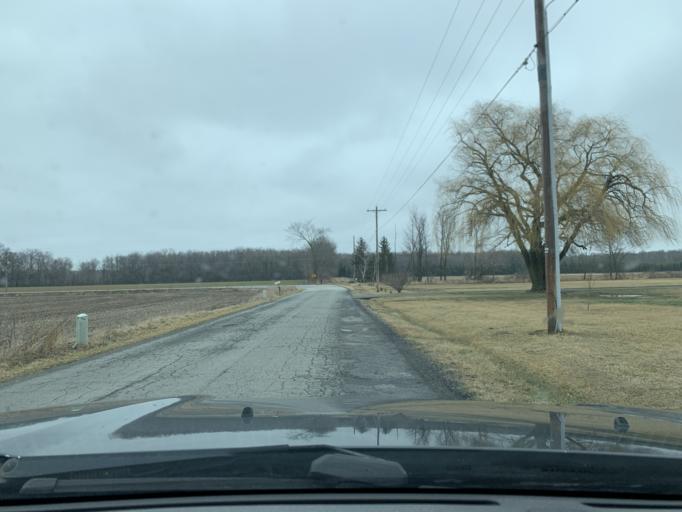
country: US
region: Indiana
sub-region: Porter County
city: Chesterton
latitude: 41.6095
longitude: -87.0044
